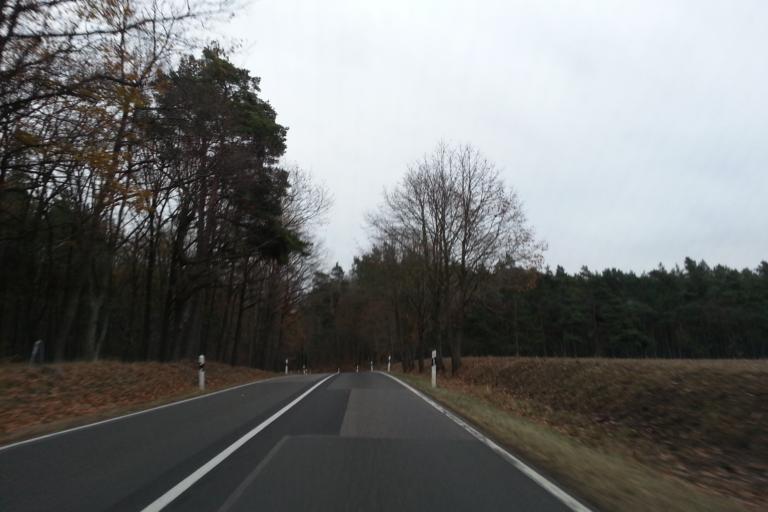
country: DE
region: Mecklenburg-Vorpommern
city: Ferdinandshof
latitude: 53.5955
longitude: 13.8363
